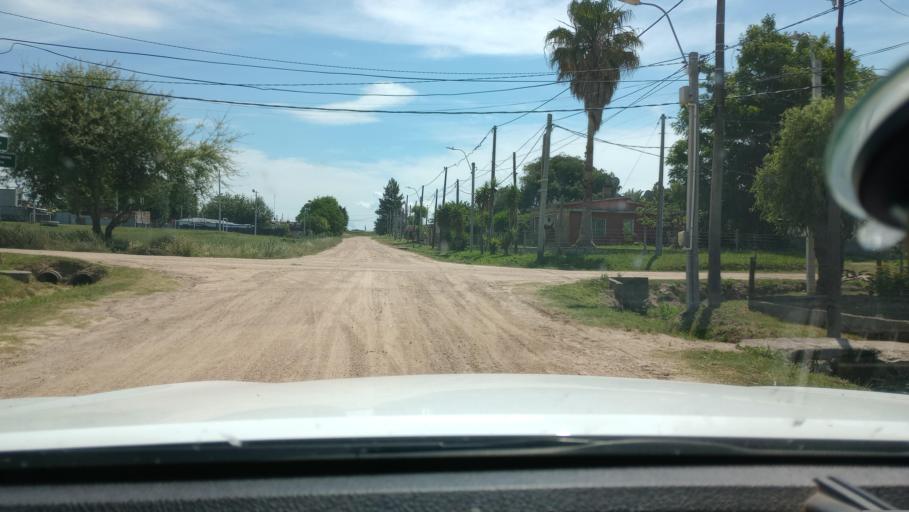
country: UY
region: Canelones
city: Joaquin Suarez
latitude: -34.7520
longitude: -56.0169
